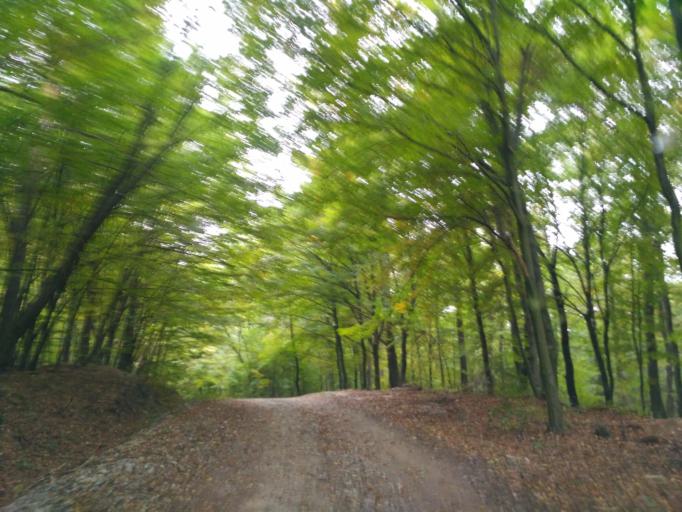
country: SK
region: Kosicky
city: Kosice
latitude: 48.7937
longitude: 21.2732
